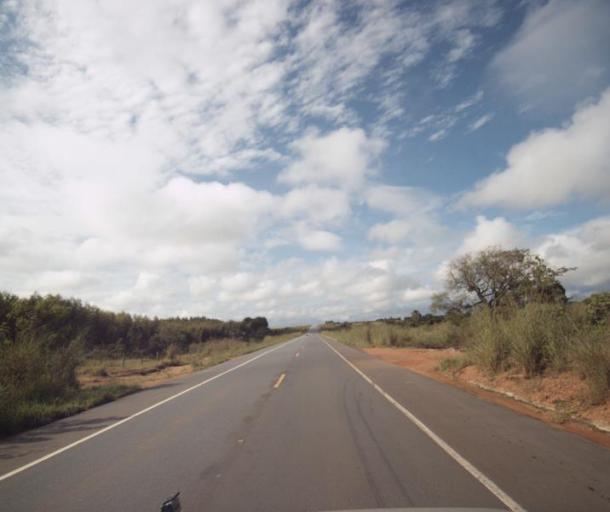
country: BR
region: Goias
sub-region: Barro Alto
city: Barro Alto
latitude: -15.2176
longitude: -48.6974
